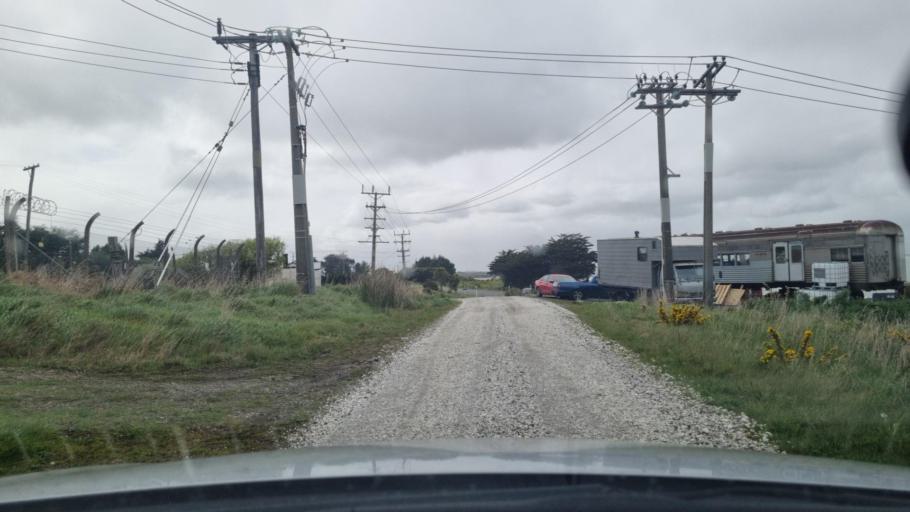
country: NZ
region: Southland
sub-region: Invercargill City
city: Bluff
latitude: -46.5851
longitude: 168.3040
